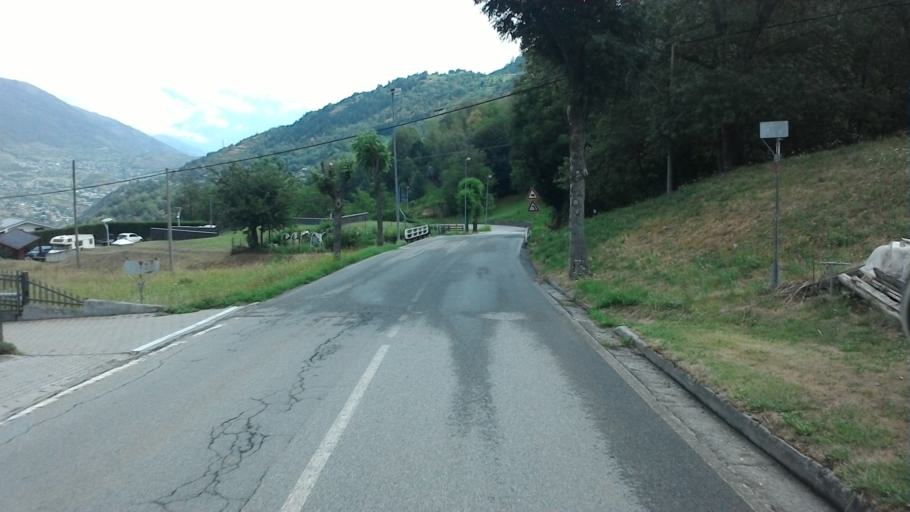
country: IT
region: Aosta Valley
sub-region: Valle d'Aosta
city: Plan d'Introd
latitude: 45.6885
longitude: 7.1873
